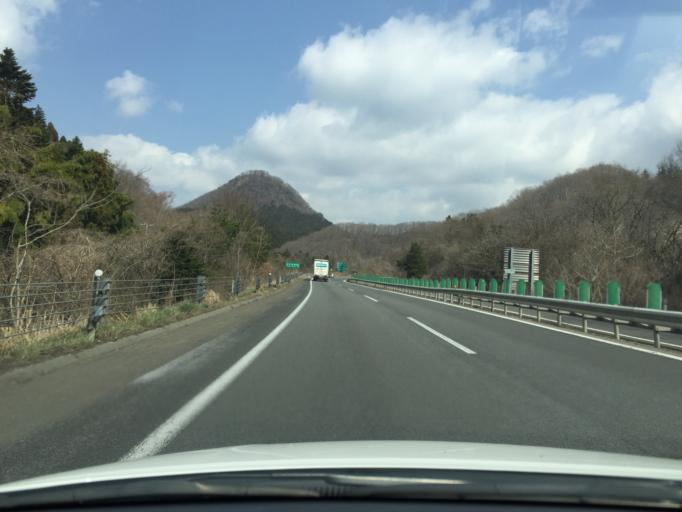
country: JP
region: Miyagi
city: Sendai
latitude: 38.2243
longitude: 140.8032
